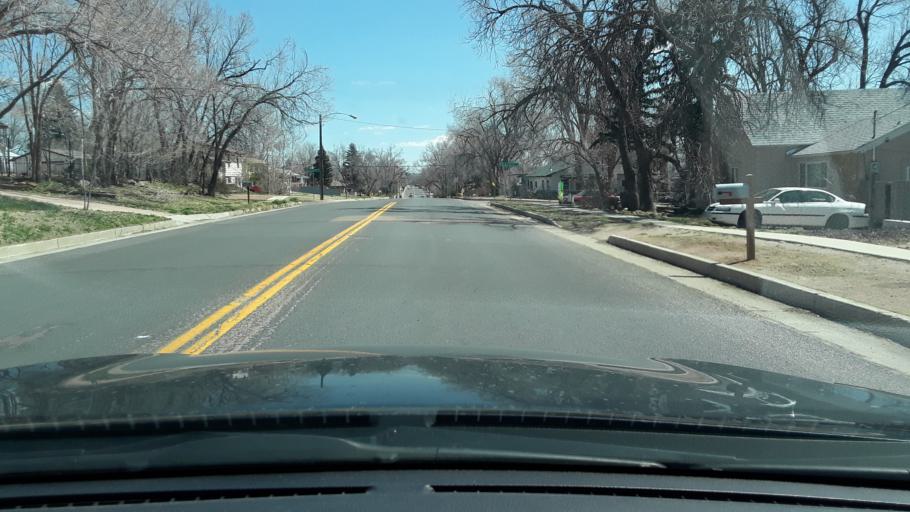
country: US
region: Colorado
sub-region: El Paso County
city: Colorado Springs
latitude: 38.8489
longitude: -104.7882
